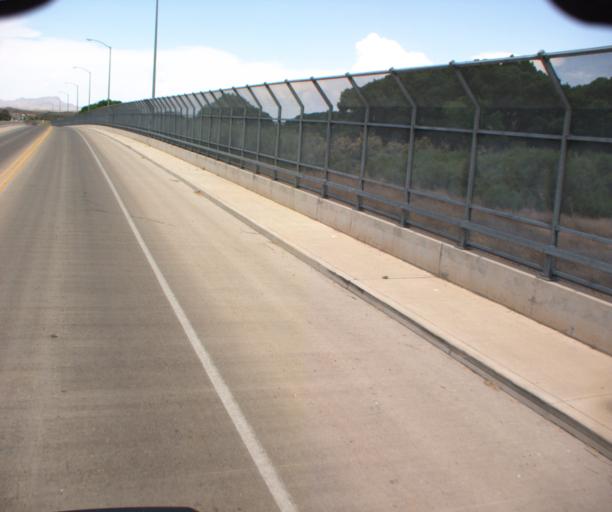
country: US
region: Arizona
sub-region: Greenlee County
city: Clifton
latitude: 32.7230
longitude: -109.1022
